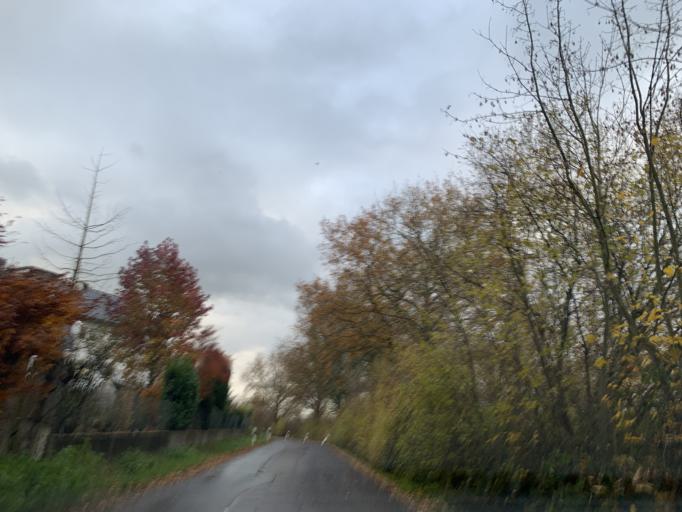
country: DE
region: North Rhine-Westphalia
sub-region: Regierungsbezirk Munster
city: Laer
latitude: 52.1089
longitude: 7.3892
